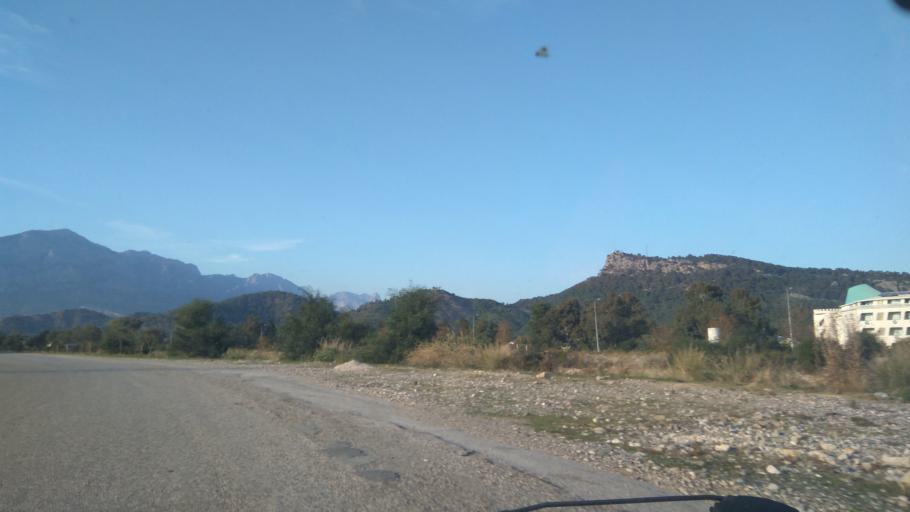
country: TR
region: Antalya
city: Kemer
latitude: 36.5646
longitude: 30.5711
